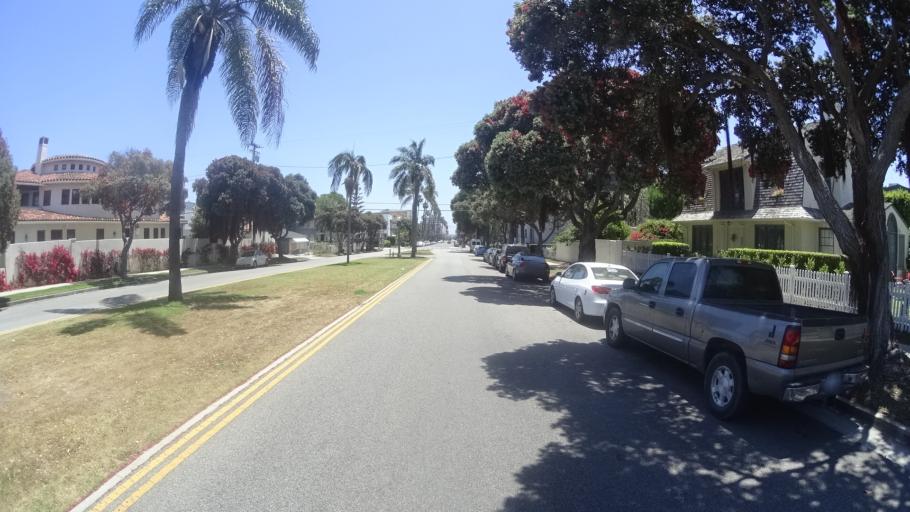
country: US
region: California
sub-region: Los Angeles County
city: Santa Monica
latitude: 34.0252
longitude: -118.5056
